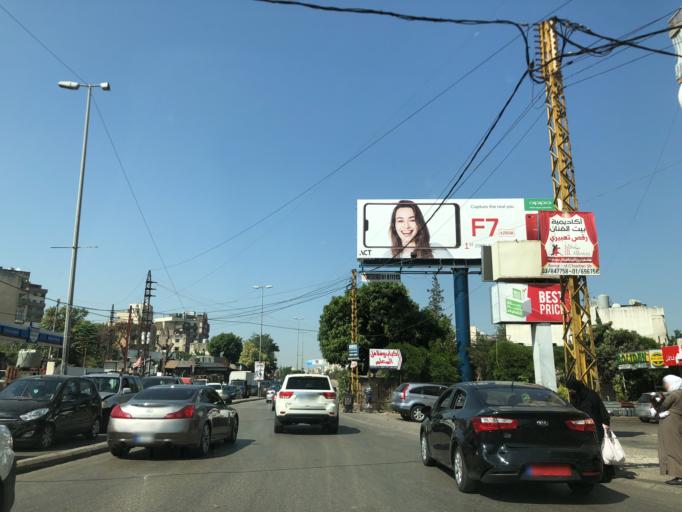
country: LB
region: Mont-Liban
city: Jdaidet el Matn
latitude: 33.8843
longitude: 35.5572
